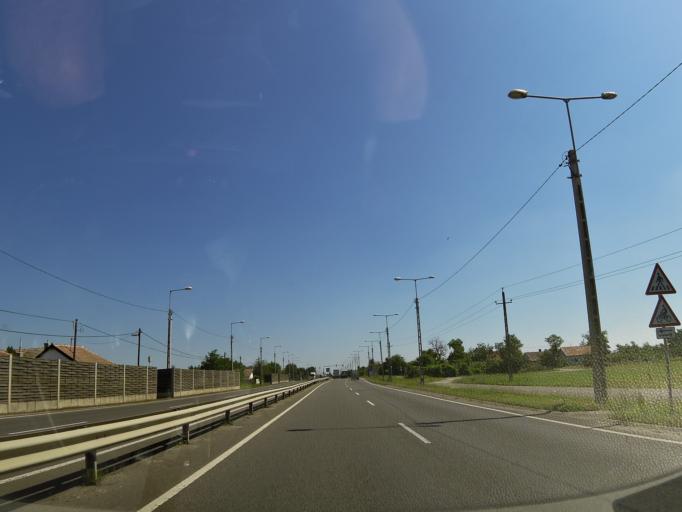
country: HU
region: Jasz-Nagykun-Szolnok
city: Torokszentmiklos
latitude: 47.2033
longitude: 20.4759
